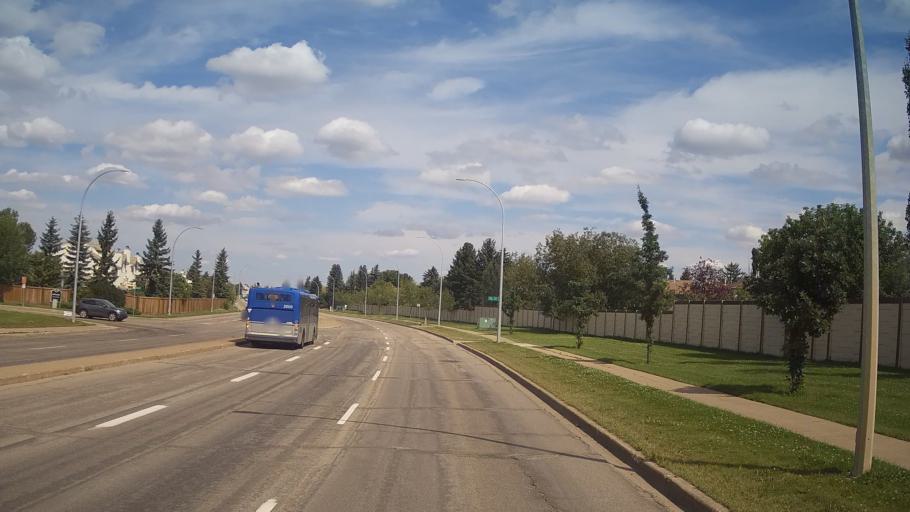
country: CA
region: Alberta
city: St. Albert
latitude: 53.5292
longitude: -113.6267
